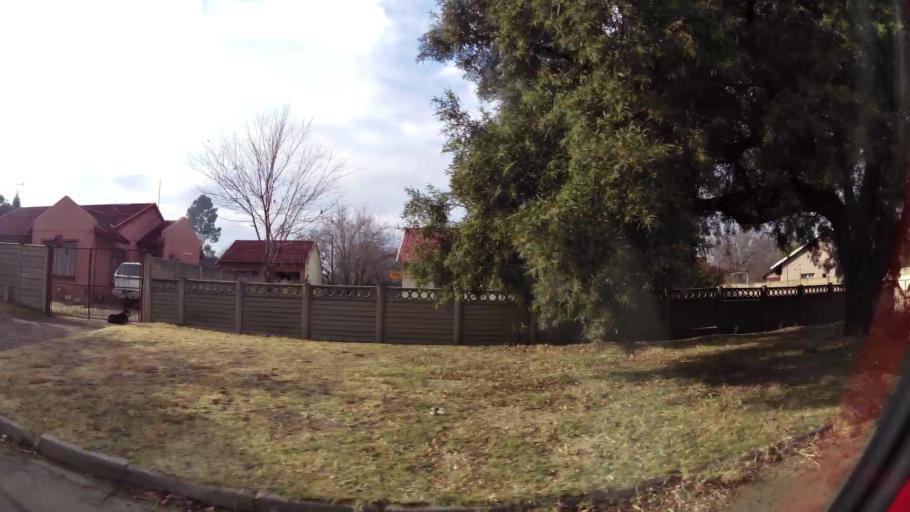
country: ZA
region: Gauteng
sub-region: Sedibeng District Municipality
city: Vanderbijlpark
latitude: -26.7040
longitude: 27.8180
